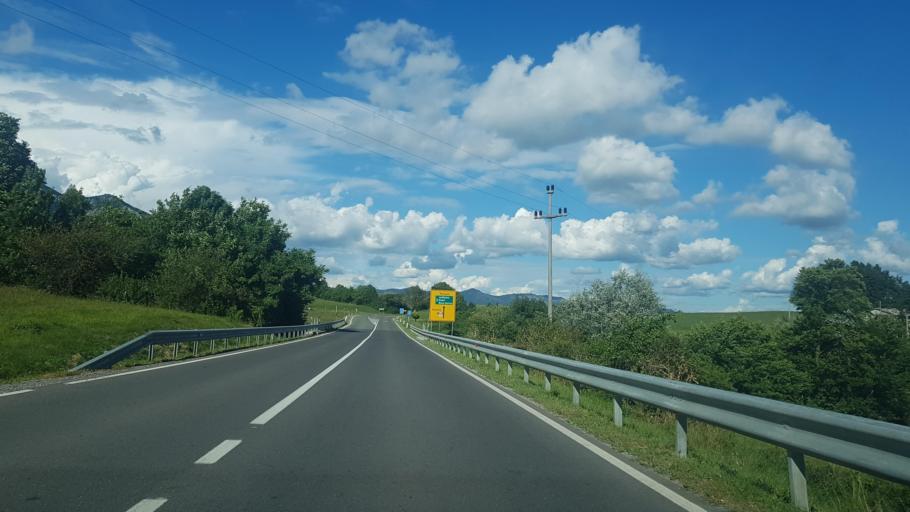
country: SI
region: Divaca
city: Divaca
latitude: 45.7553
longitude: 14.0666
